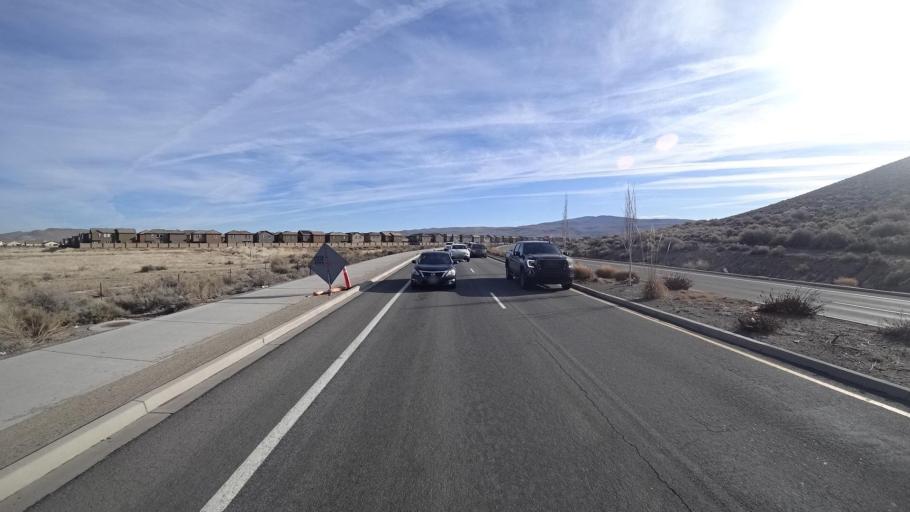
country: US
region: Nevada
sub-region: Washoe County
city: Spanish Springs
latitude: 39.6055
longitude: -119.7051
